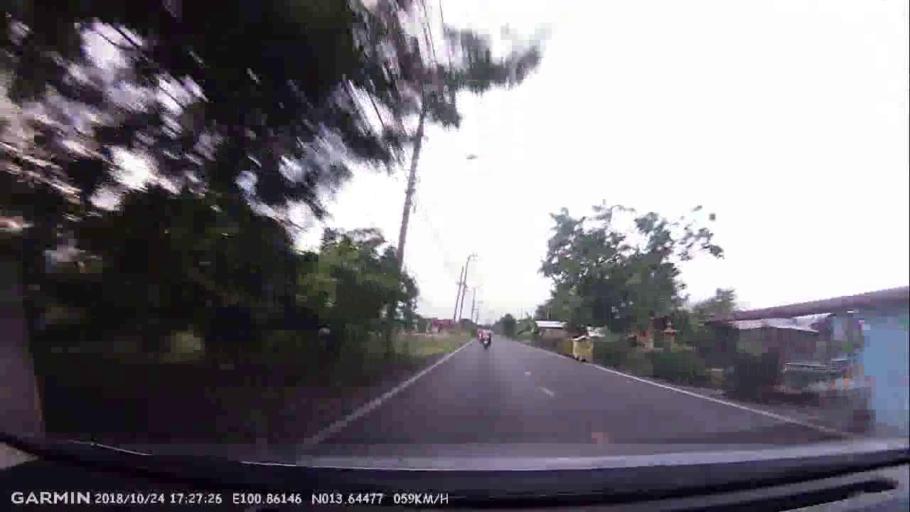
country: TH
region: Samut Prakan
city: Ban Khlong Bang Sao Thong
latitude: 13.6448
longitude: 100.8614
